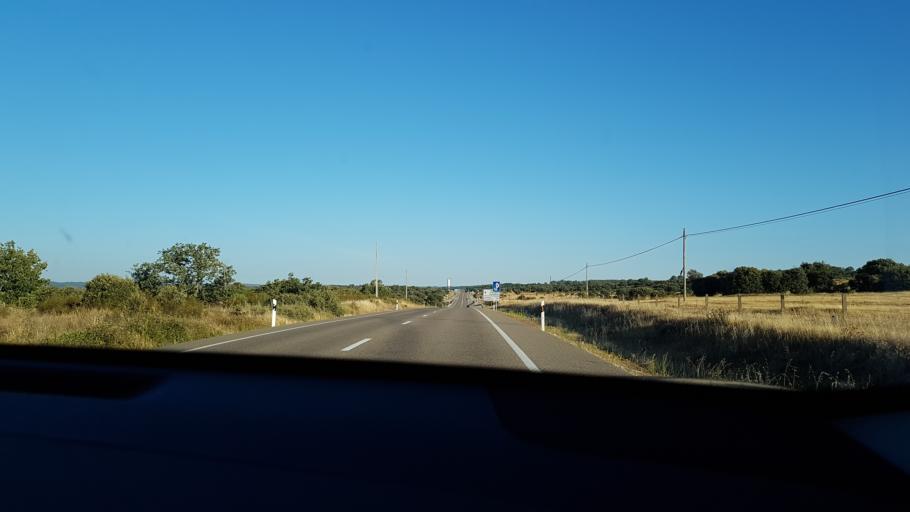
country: ES
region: Castille and Leon
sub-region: Provincia de Zamora
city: Fonfria
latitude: 41.6425
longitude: -6.1529
